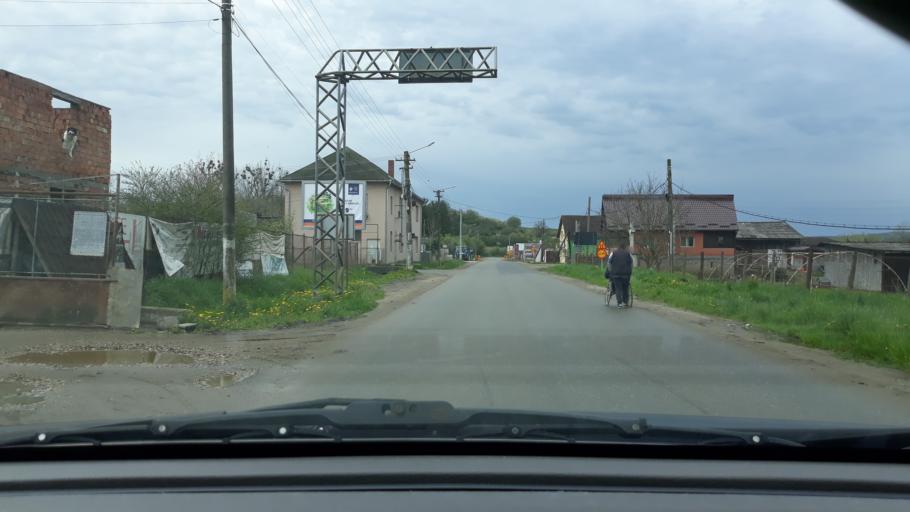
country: RO
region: Salaj
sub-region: Comuna Cehu Silvaniei
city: Cehu Silvaniei
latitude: 47.4052
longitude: 23.1623
